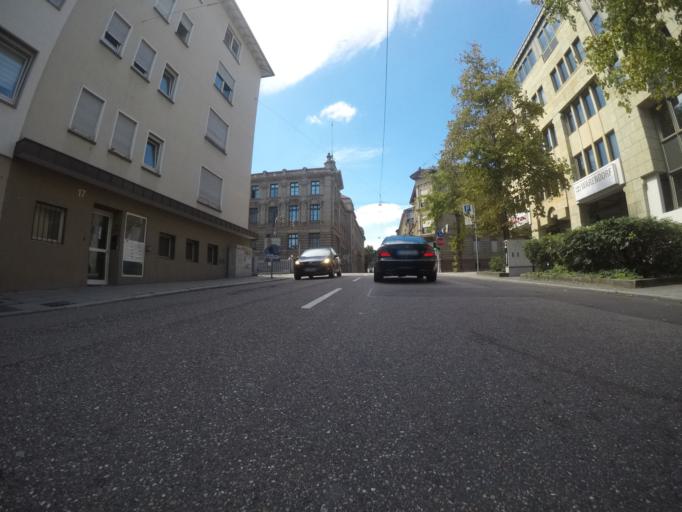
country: DE
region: Baden-Wuerttemberg
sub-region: Regierungsbezirk Stuttgart
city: Stuttgart
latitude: 48.7713
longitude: 9.1693
